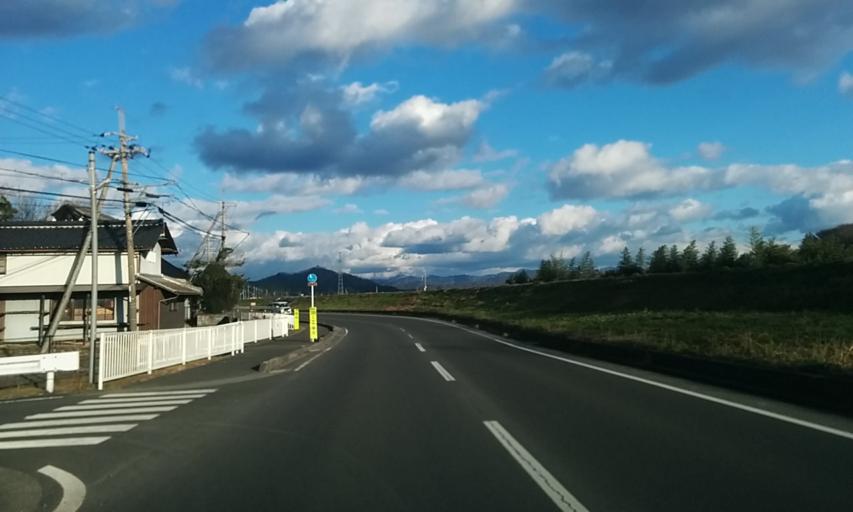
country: JP
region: Kyoto
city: Ayabe
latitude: 35.3102
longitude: 135.2058
